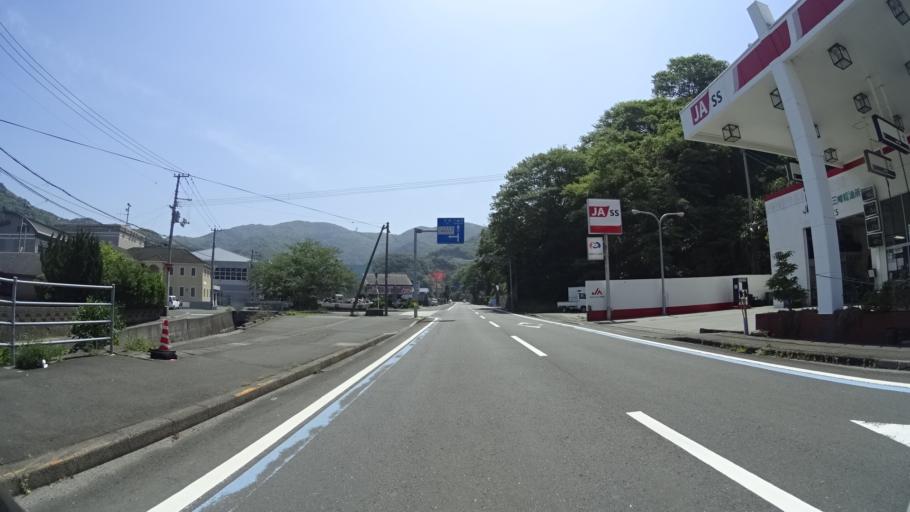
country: JP
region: Ehime
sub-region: Nishiuwa-gun
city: Ikata-cho
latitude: 33.3873
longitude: 132.1227
